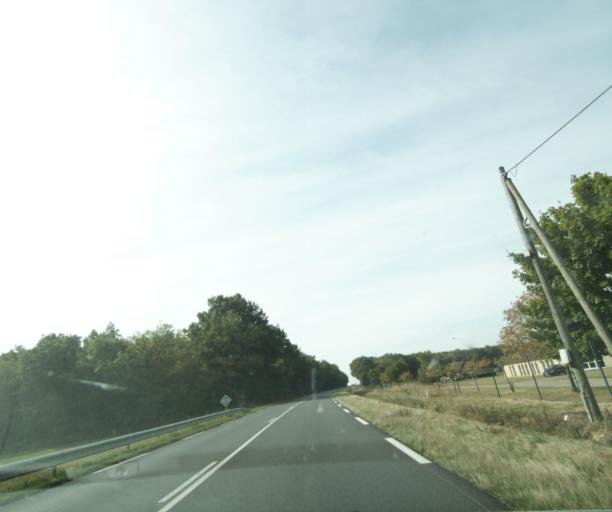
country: FR
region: Auvergne
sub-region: Departement de l'Allier
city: Saint-Francois
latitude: 46.4416
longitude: 3.9119
